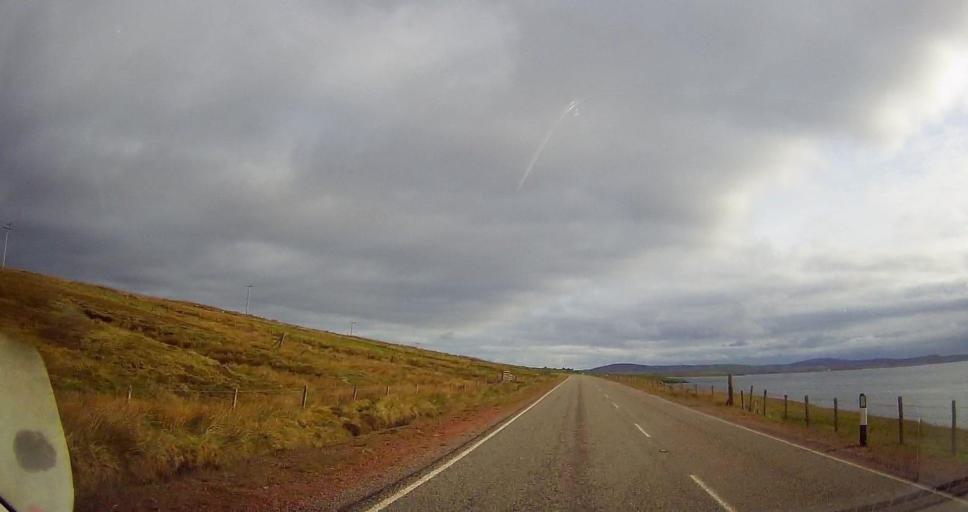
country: GB
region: Scotland
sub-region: Shetland Islands
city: Lerwick
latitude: 60.4582
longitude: -1.2102
